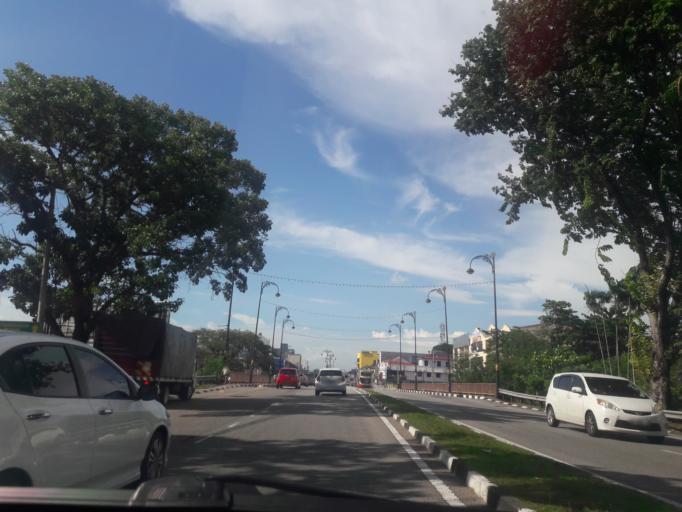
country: MY
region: Kedah
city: Sungai Petani
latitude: 5.6384
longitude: 100.4886
